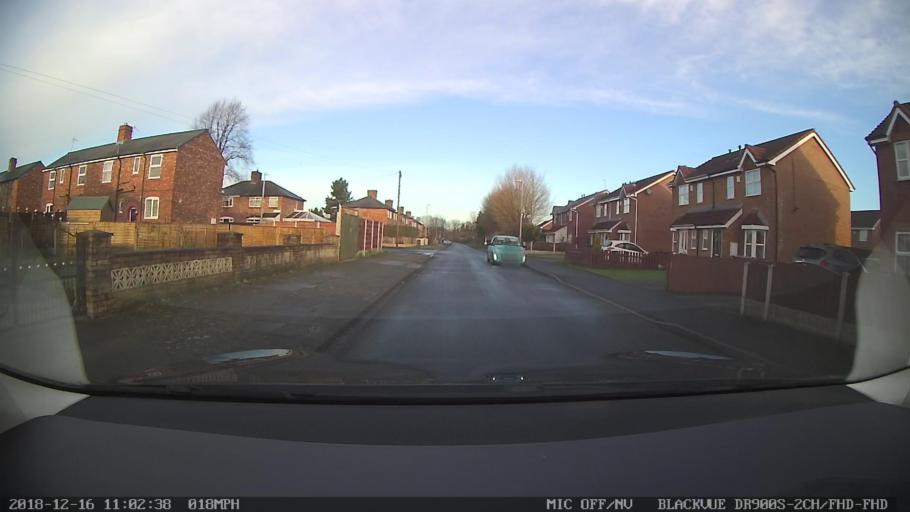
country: GB
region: England
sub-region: Manchester
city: Swinton
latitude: 53.4801
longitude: -2.3703
